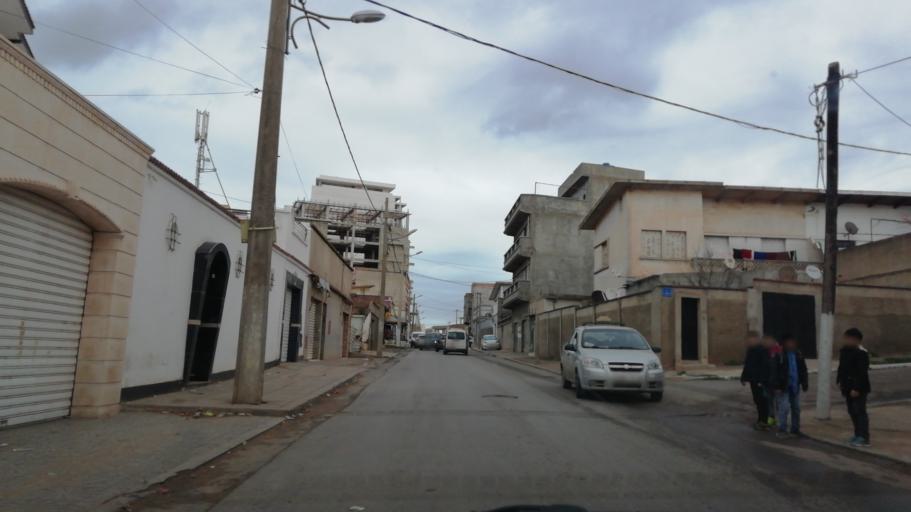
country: DZ
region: Oran
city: Oran
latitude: 35.6931
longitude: -0.6053
